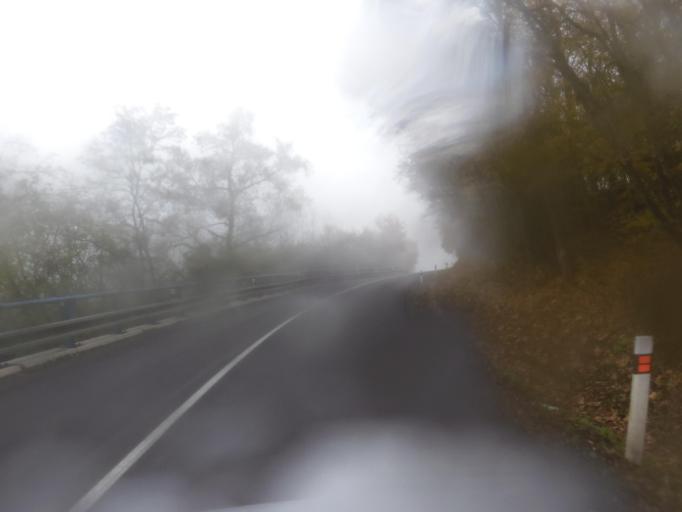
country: CZ
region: Ustecky
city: Zatec
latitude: 50.3108
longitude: 13.6124
